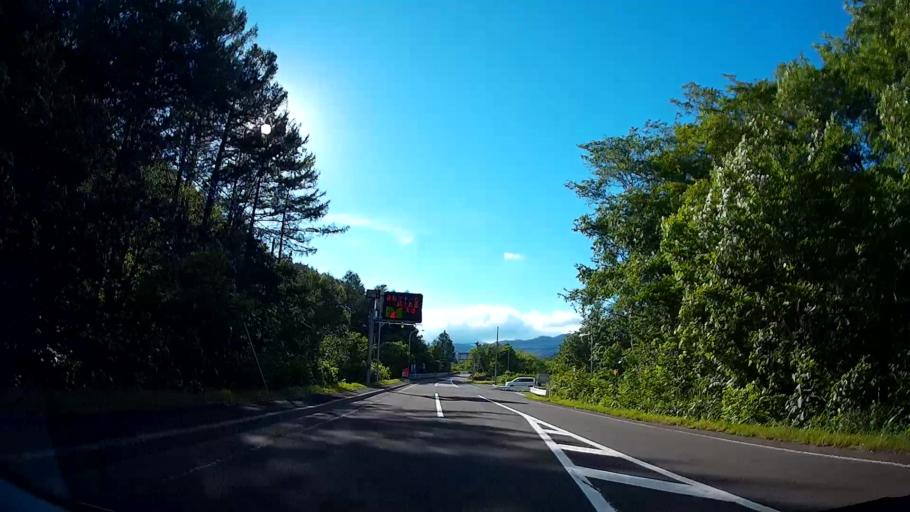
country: JP
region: Hokkaido
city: Sapporo
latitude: 42.9758
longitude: 141.1392
